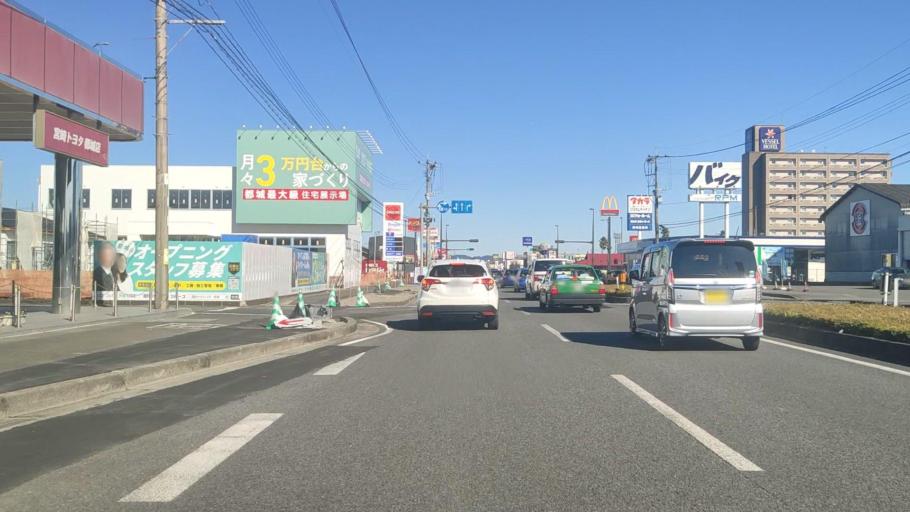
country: JP
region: Miyazaki
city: Miyakonojo
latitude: 31.7573
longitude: 131.0836
